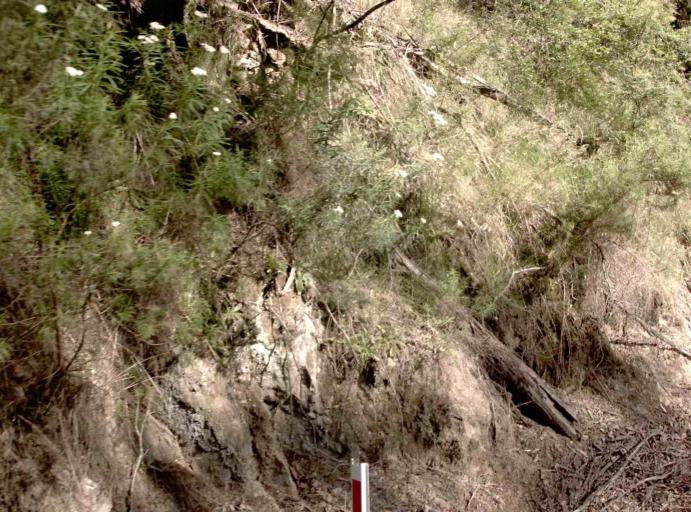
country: AU
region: Victoria
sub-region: East Gippsland
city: Lakes Entrance
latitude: -37.5023
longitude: 148.5434
